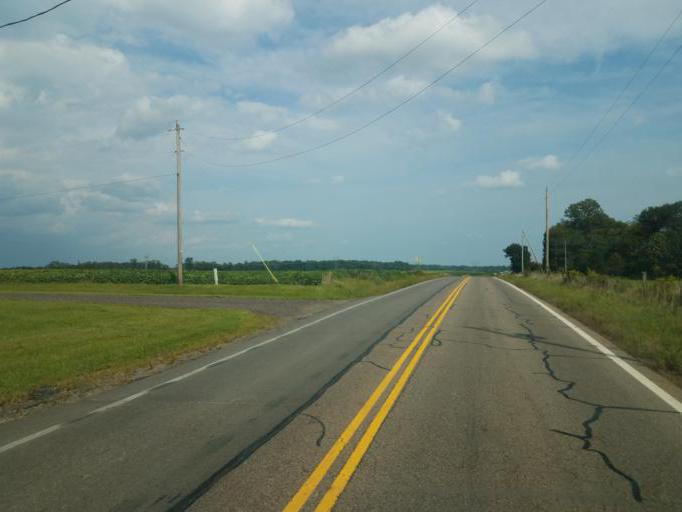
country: US
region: Ohio
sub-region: Knox County
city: Gambier
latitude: 40.3558
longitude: -82.3275
